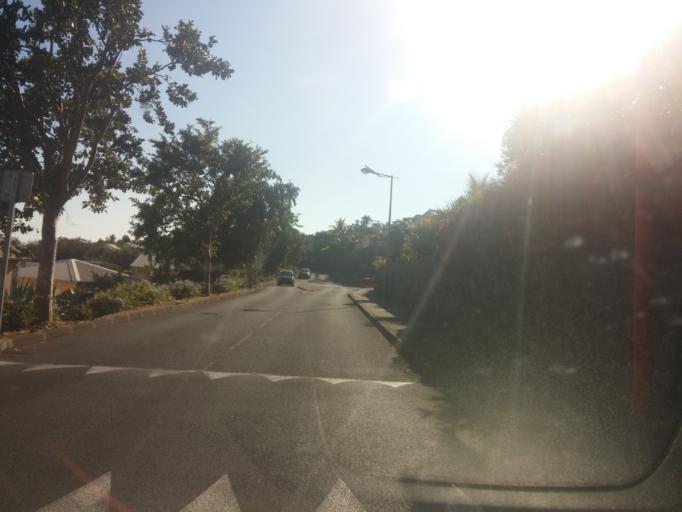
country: RE
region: Reunion
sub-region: Reunion
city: La Possession
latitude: -20.9598
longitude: 55.3323
